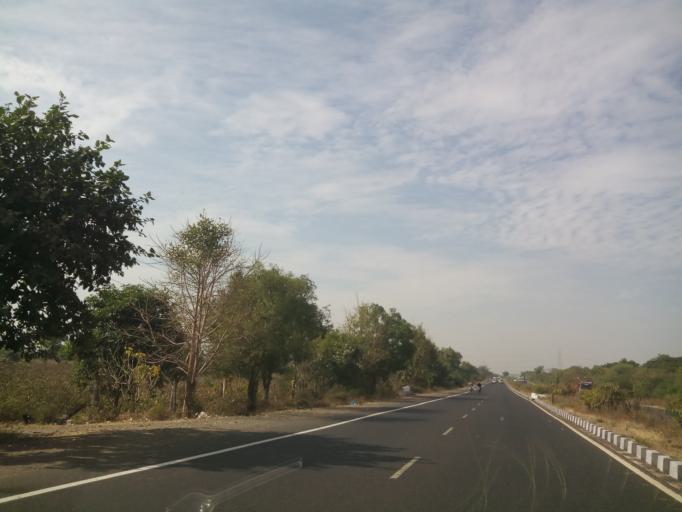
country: IN
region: Gujarat
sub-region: Rajkot
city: Rajkot
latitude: 22.3433
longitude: 70.9183
